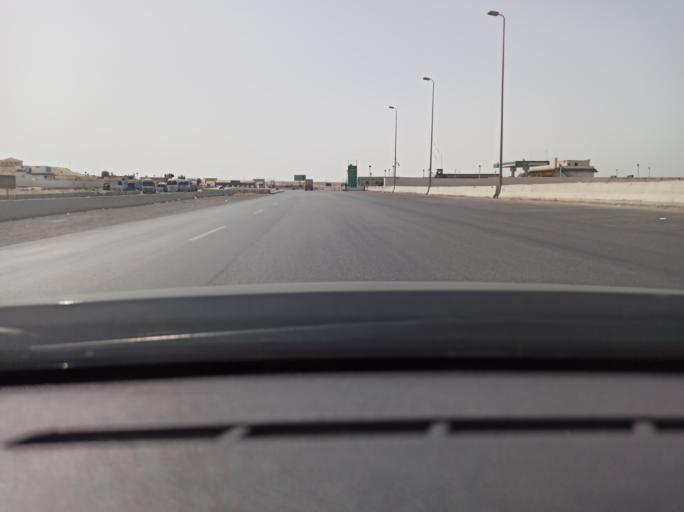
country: EG
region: Muhafazat al Qahirah
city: Halwan
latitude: 29.7095
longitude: 31.4092
